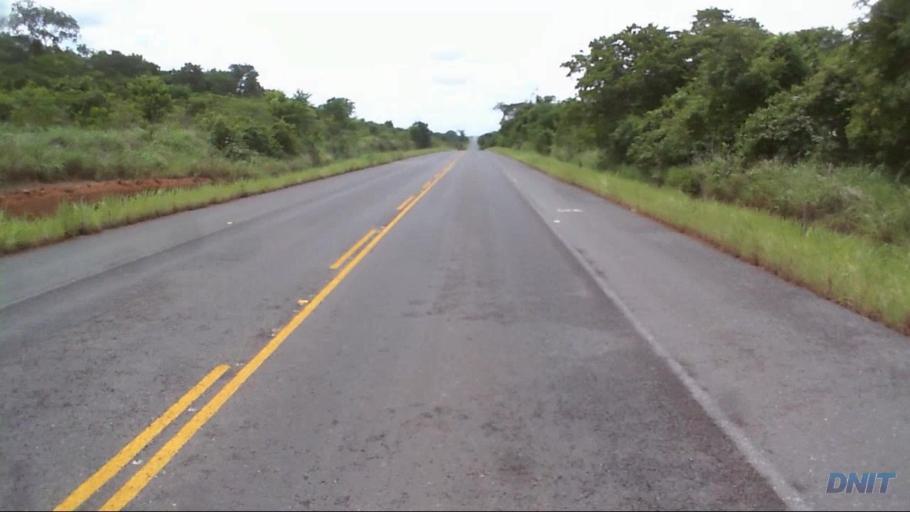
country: BR
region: Goias
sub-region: Sao Miguel Do Araguaia
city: Sao Miguel do Araguaia
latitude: -13.2993
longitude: -50.3139
